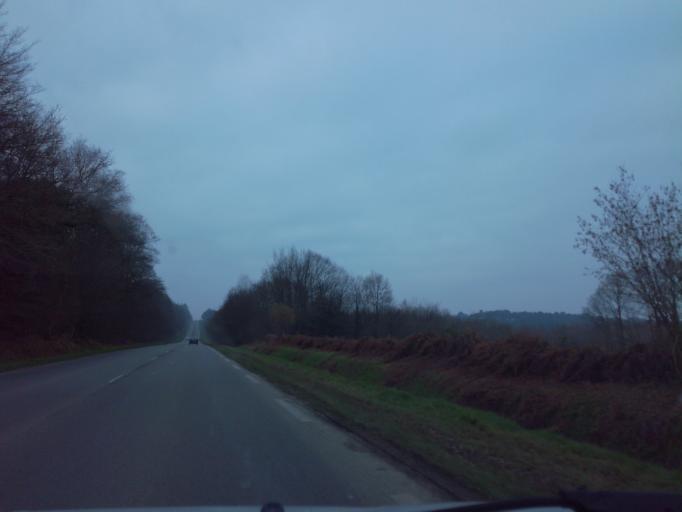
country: FR
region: Brittany
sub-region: Departement d'Ille-et-Vilaine
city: Gosne
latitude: 48.2346
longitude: -1.4692
